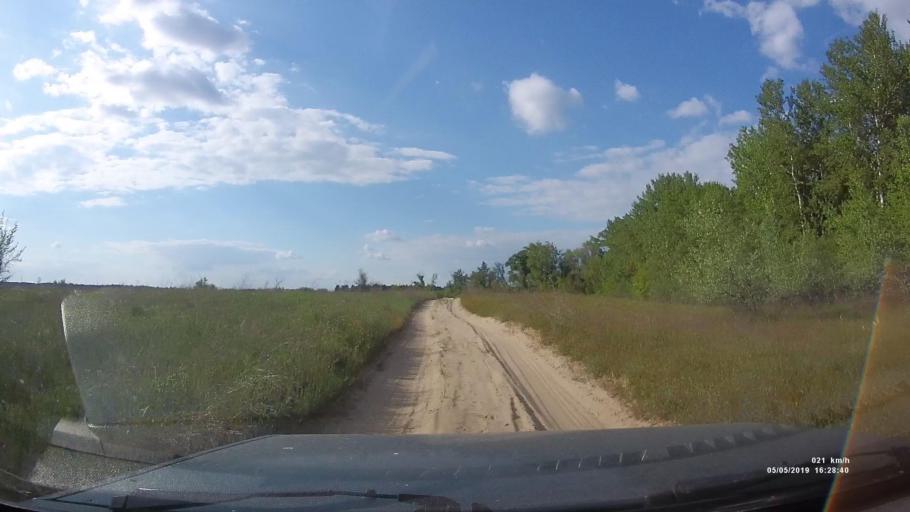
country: RU
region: Rostov
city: Ust'-Donetskiy
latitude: 47.7682
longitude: 41.0157
